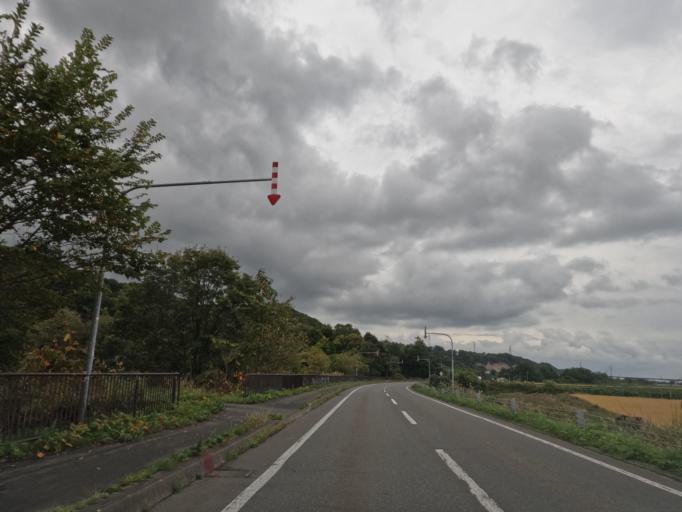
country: JP
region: Hokkaido
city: Date
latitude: 42.5158
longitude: 140.8639
